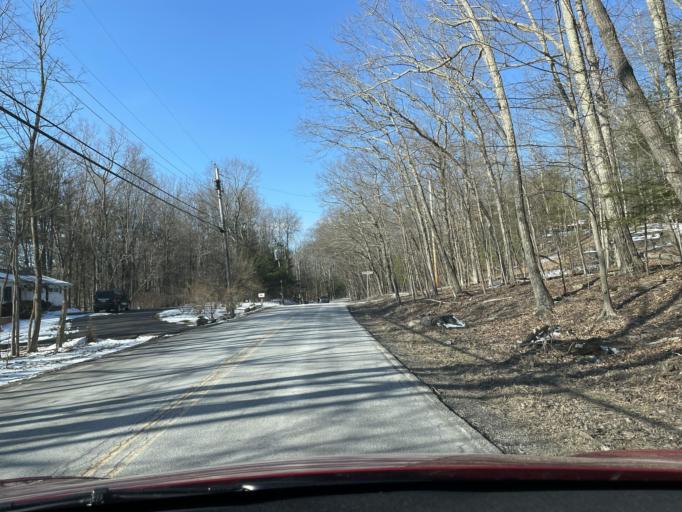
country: US
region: New York
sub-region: Ulster County
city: Woodstock
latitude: 42.0501
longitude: -74.1097
